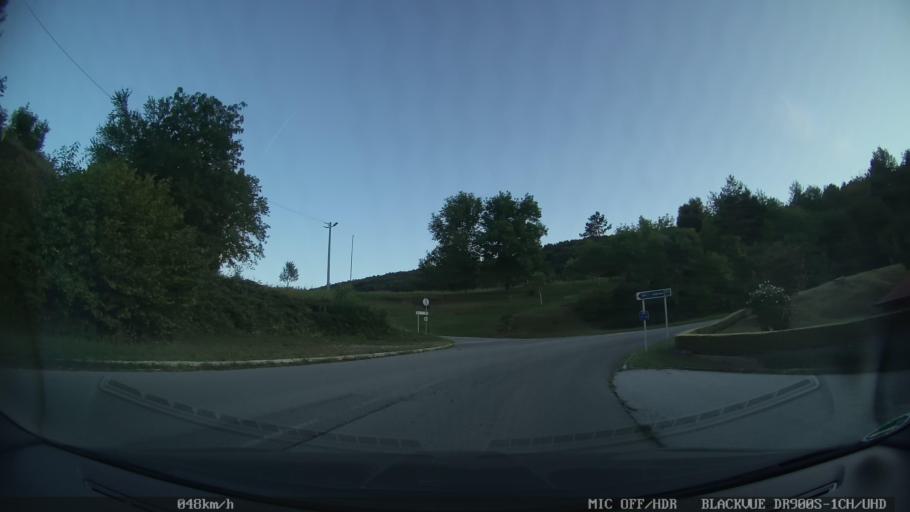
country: HR
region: Karlovacka
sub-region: Grad Ogulin
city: Ogulin
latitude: 45.2674
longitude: 15.1917
